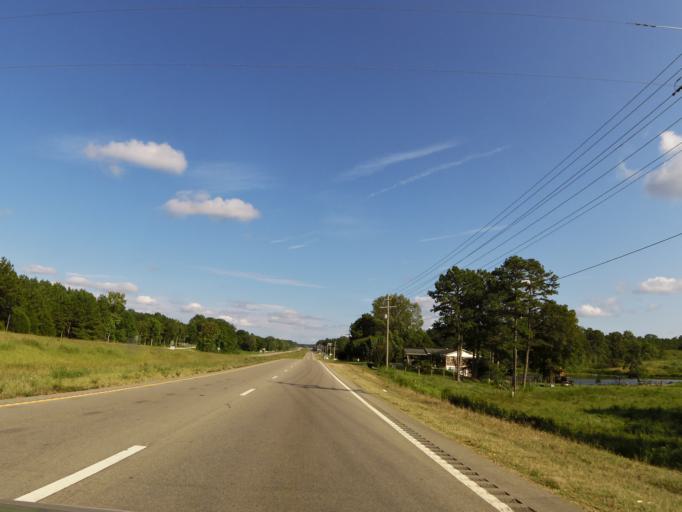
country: US
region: Mississippi
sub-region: Alcorn County
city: Farmington
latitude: 34.8768
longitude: -88.4384
